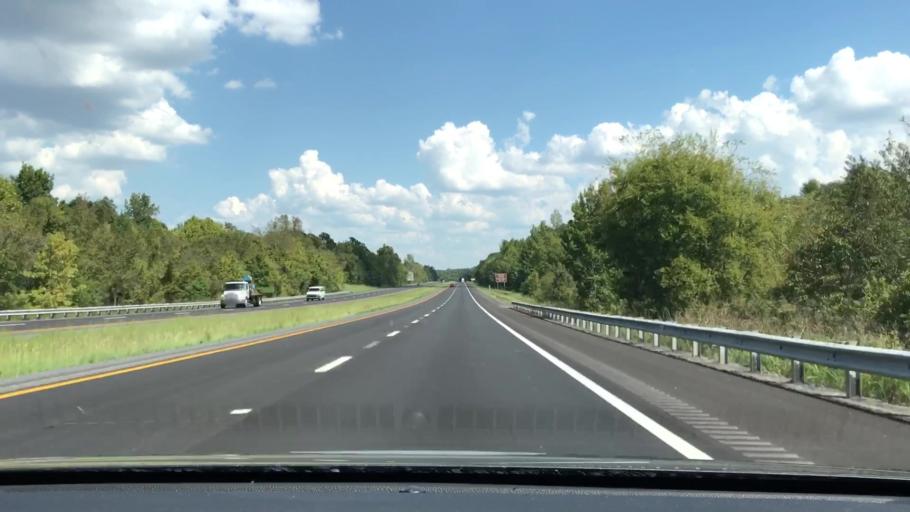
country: US
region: Kentucky
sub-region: Lyon County
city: Eddyville
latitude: 37.0881
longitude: -88.0595
